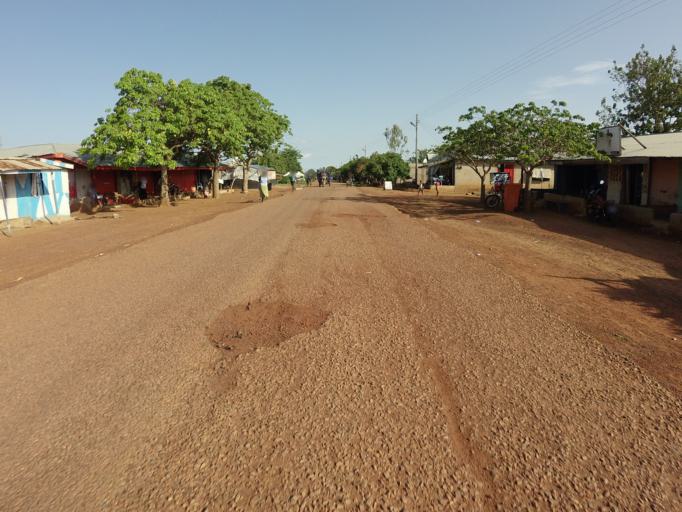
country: GH
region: Upper East
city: Bawku
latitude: 10.6302
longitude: -0.1803
